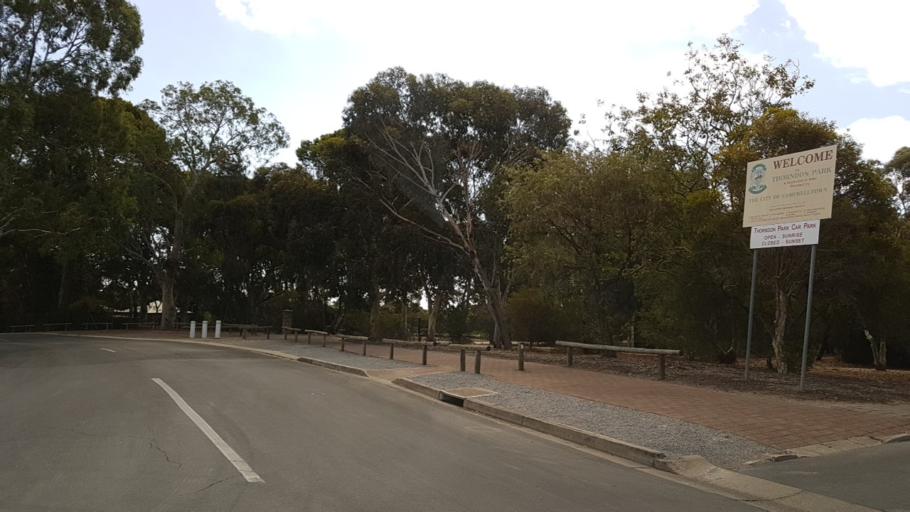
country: AU
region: South Australia
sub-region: Campbelltown
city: Athelstone
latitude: -34.8754
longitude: 138.6911
